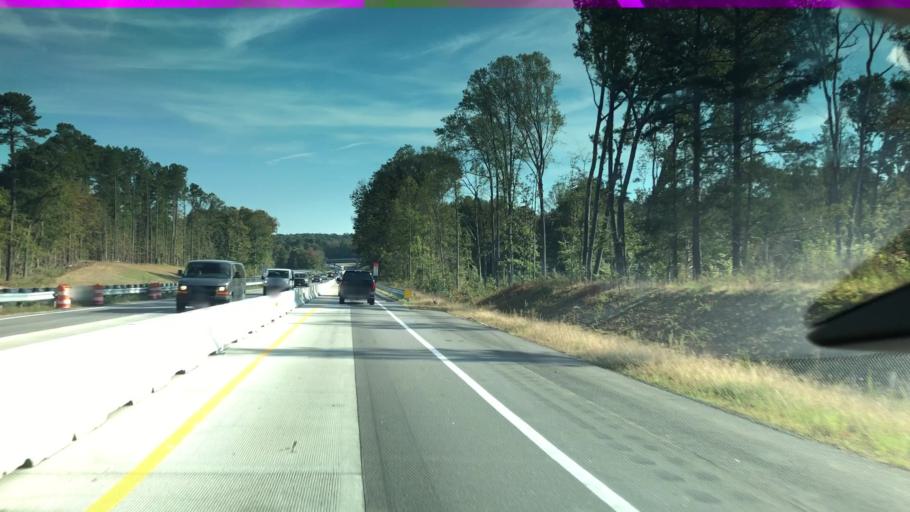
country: US
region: North Carolina
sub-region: Vance County
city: Henderson
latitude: 36.3655
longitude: -78.3683
